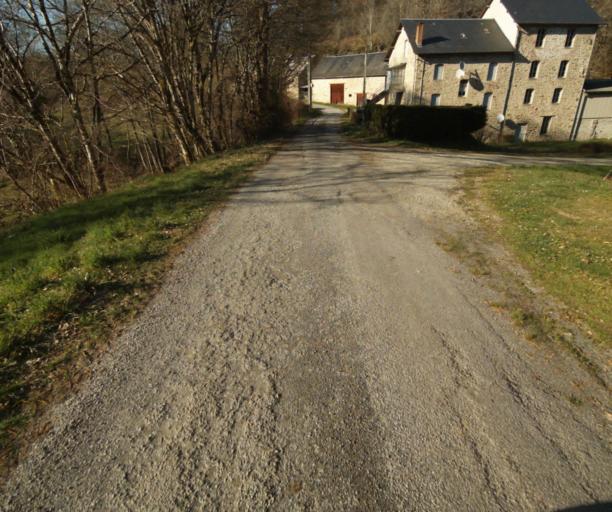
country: FR
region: Limousin
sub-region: Departement de la Correze
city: Chamboulive
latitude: 45.4913
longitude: 1.7275
